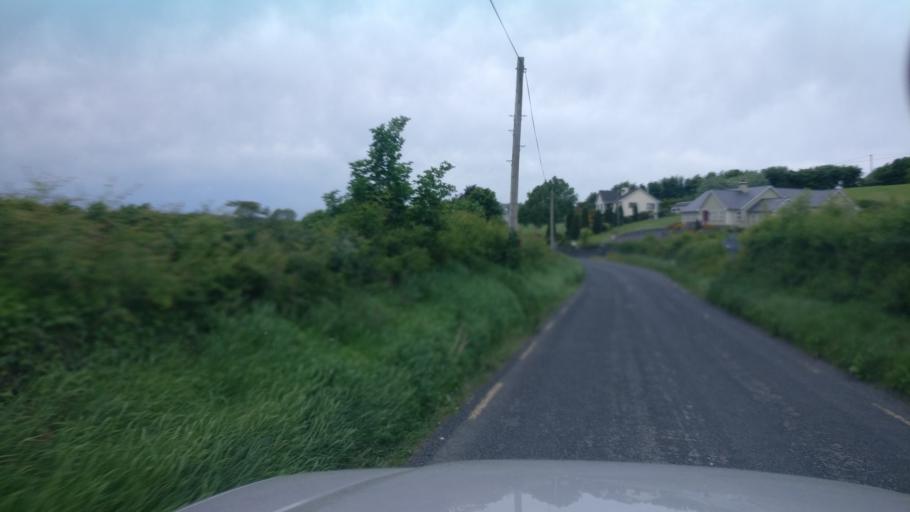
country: IE
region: Connaught
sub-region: County Galway
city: Portumna
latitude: 53.1146
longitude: -8.2982
